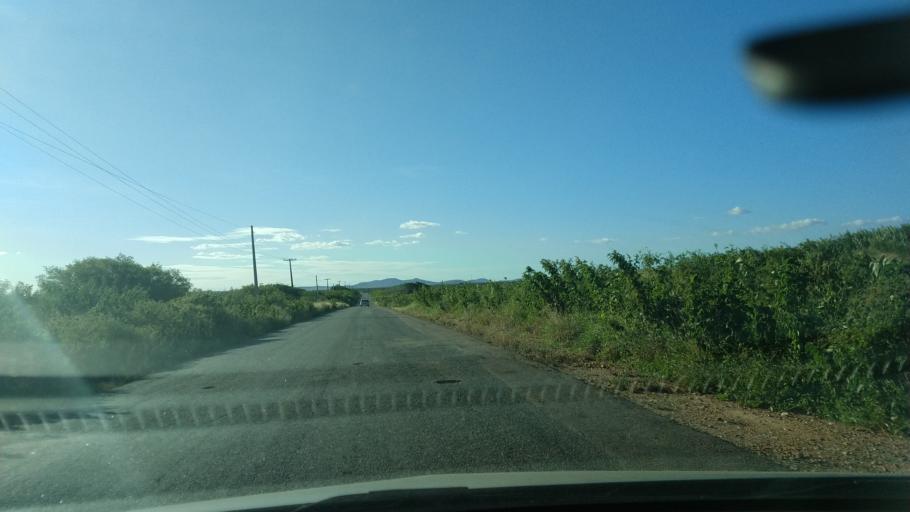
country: BR
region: Rio Grande do Norte
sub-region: Sao Jose Do Campestre
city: Sao Jose do Campestre
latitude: -6.3998
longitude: -35.6558
